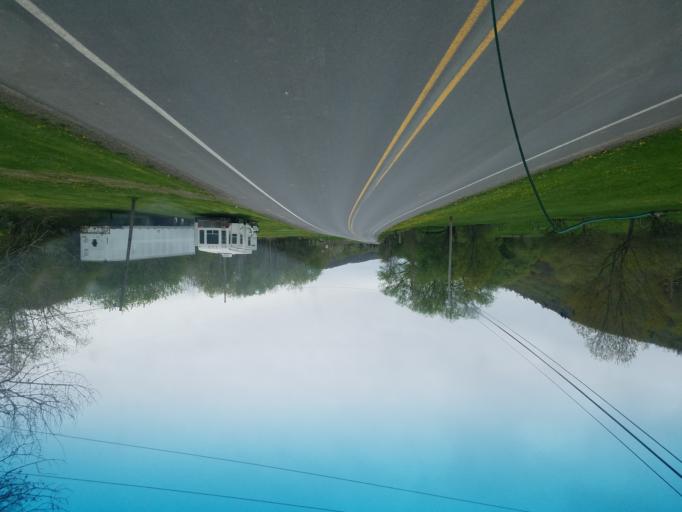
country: US
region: Pennsylvania
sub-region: Tioga County
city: Westfield
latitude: 41.9328
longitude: -77.6326
